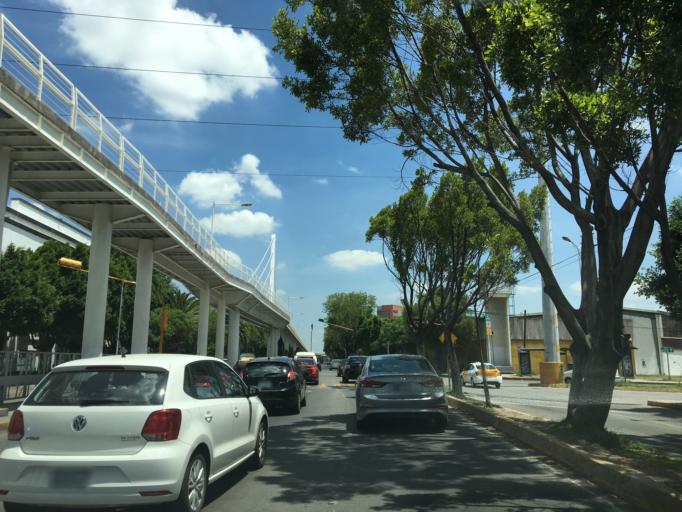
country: MX
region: Puebla
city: Puebla
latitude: 19.0598
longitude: -98.2197
